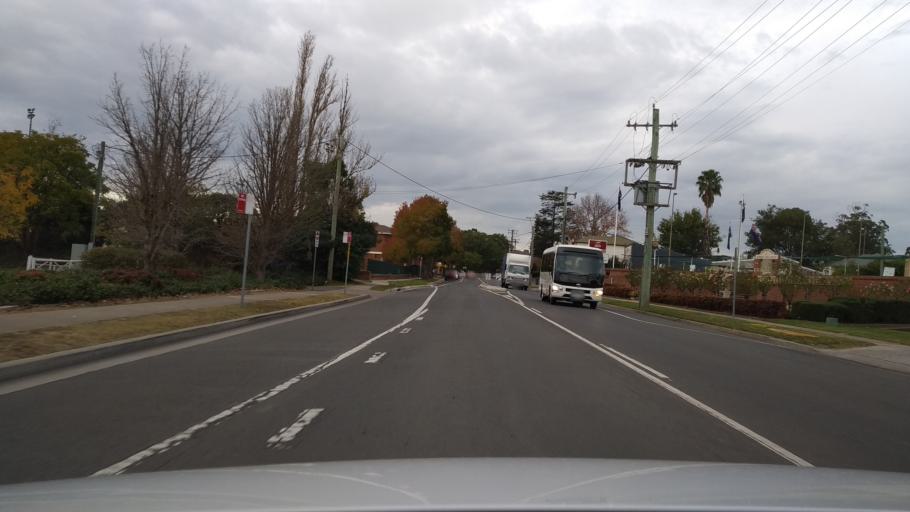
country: AU
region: New South Wales
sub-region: Camden
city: Elderslie
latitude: -34.0575
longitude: 150.6915
